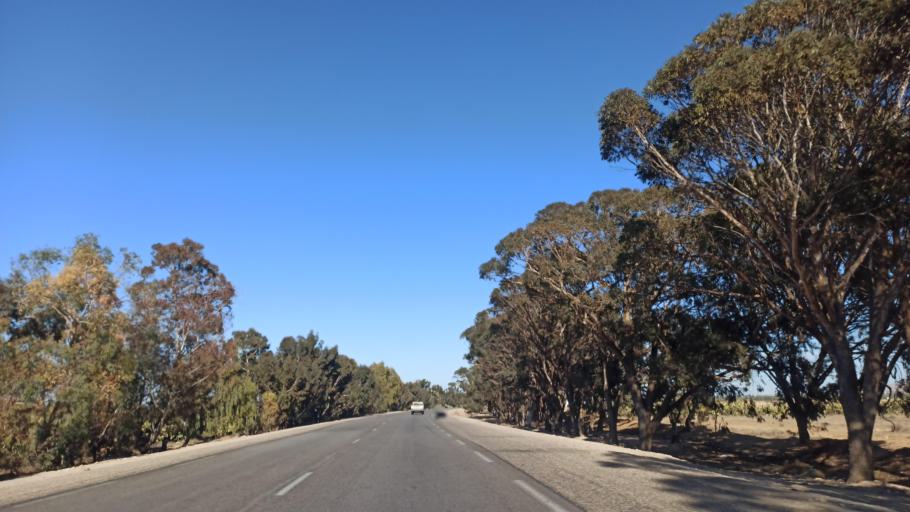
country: TN
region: Sidi Bu Zayd
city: Jilma
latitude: 35.2318
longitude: 9.3853
